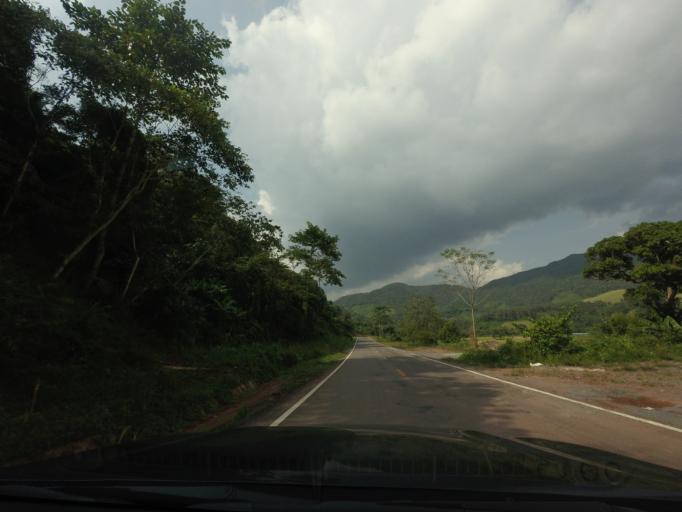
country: TH
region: Nan
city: Bo Kluea
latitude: 19.2258
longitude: 101.1824
